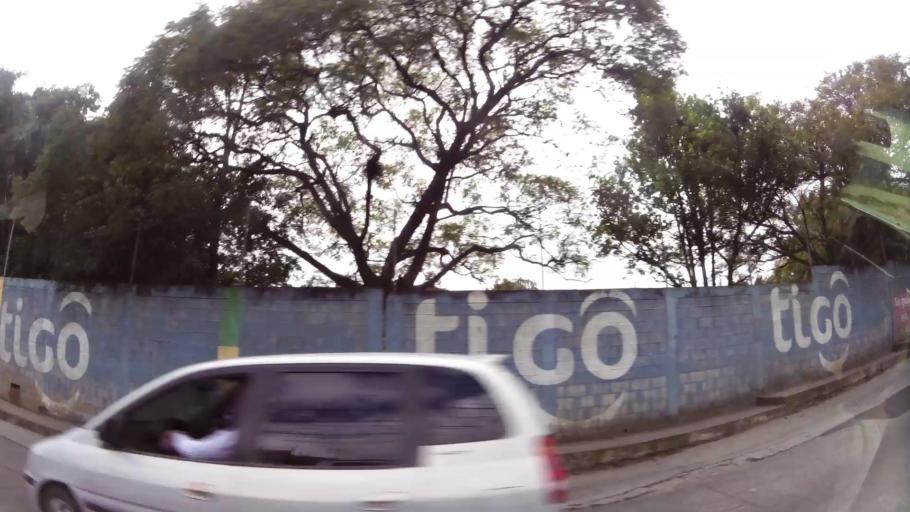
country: GT
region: Guatemala
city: Mixco
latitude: 14.6399
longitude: -90.5988
